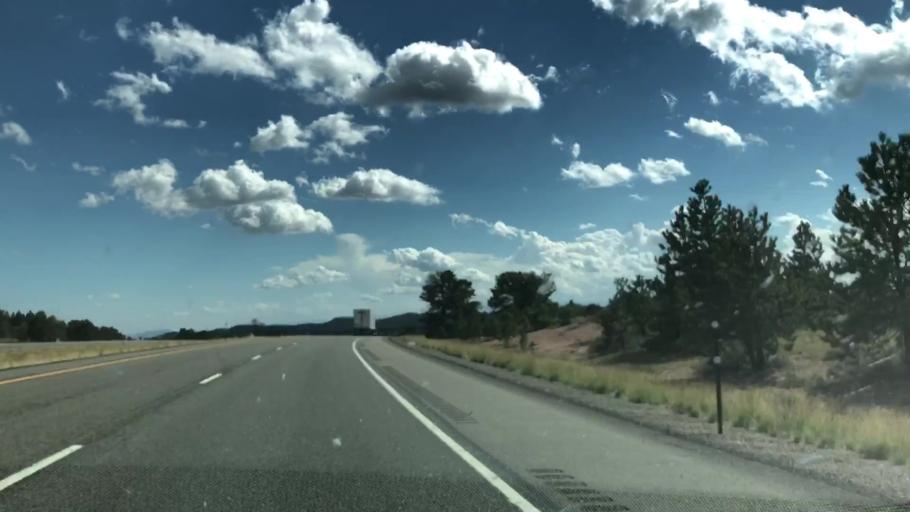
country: US
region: Wyoming
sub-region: Albany County
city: Laramie
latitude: 41.0139
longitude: -105.4202
